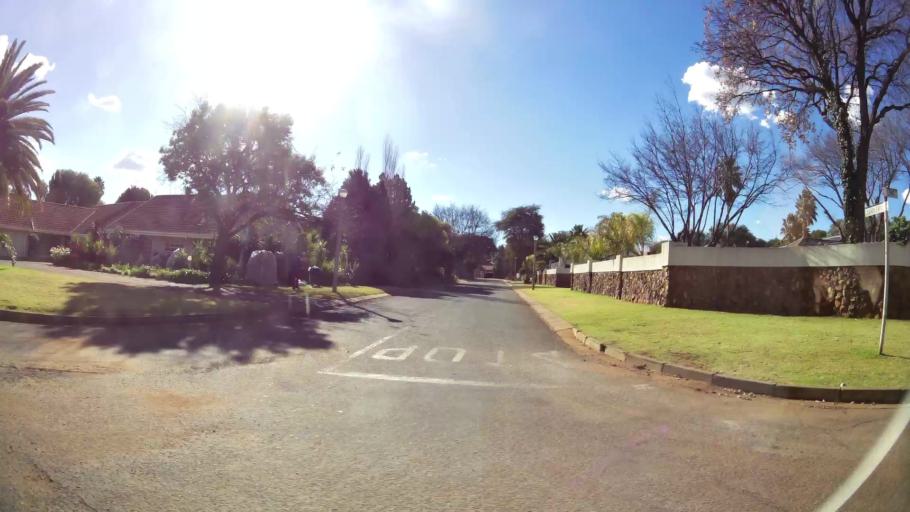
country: ZA
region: North-West
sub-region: Dr Kenneth Kaunda District Municipality
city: Klerksdorp
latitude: -26.8283
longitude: 26.6693
